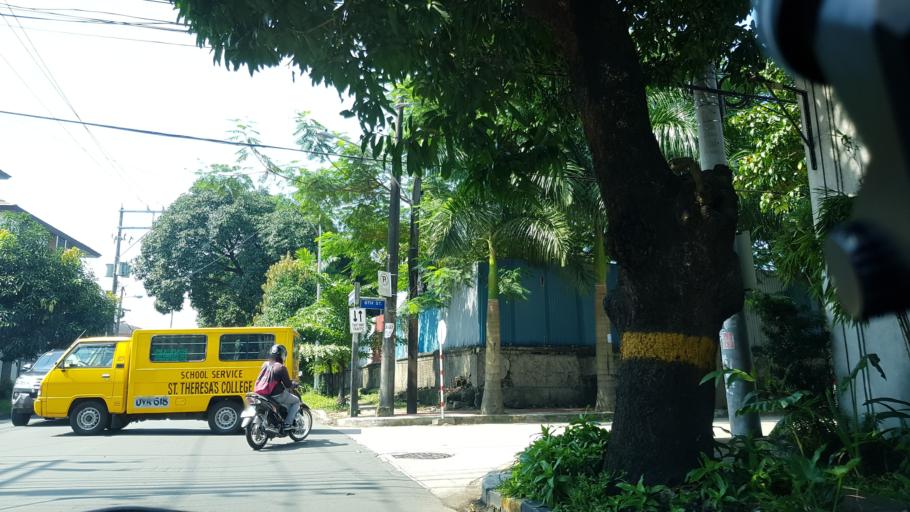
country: PH
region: Metro Manila
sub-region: San Juan
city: San Juan
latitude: 14.6155
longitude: 121.0307
